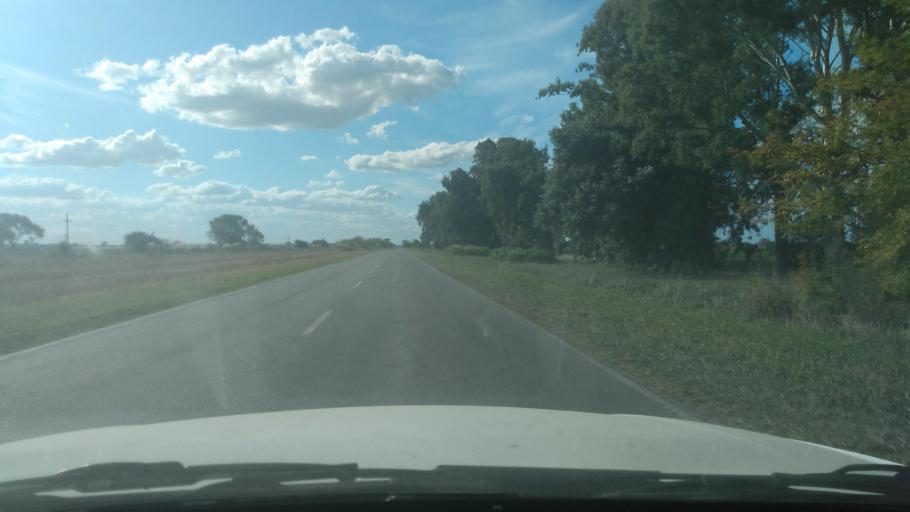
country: AR
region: Buenos Aires
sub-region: Partido de Navarro
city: Navarro
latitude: -34.9789
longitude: -59.3164
